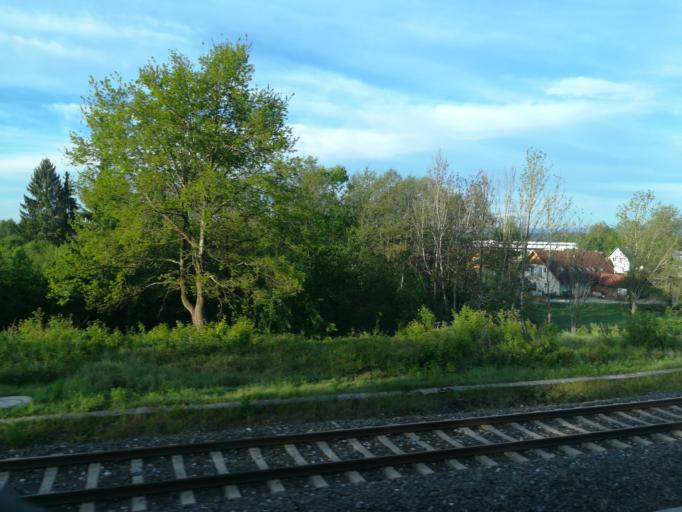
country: AT
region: Styria
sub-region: Politischer Bezirk Graz-Umgebung
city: Lieboch
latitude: 46.9713
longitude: 15.3382
